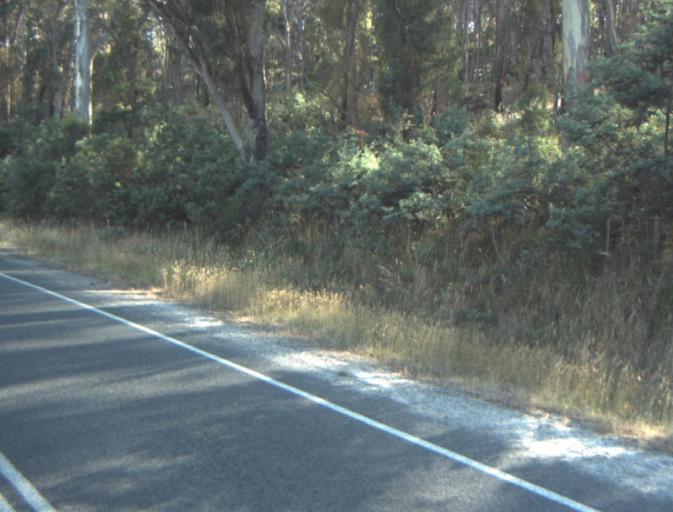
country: AU
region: Tasmania
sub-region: Launceston
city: Newstead
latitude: -41.4262
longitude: 147.2550
